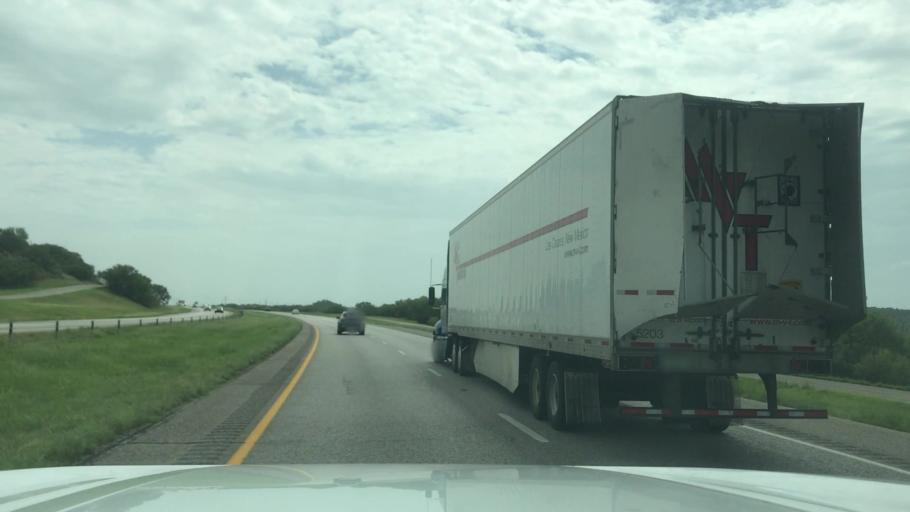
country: US
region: Texas
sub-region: Callahan County
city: Baird
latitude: 32.3702
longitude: -99.2146
